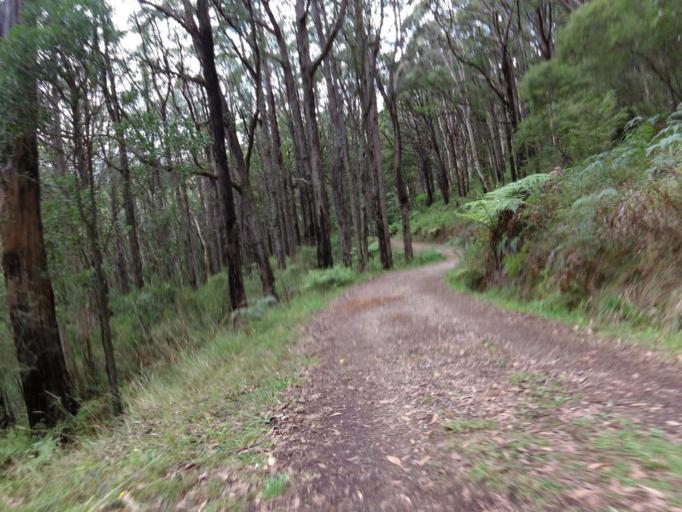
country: AU
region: Victoria
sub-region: Yarra Ranges
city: Ferny Creek
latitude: -37.8655
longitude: 145.3378
